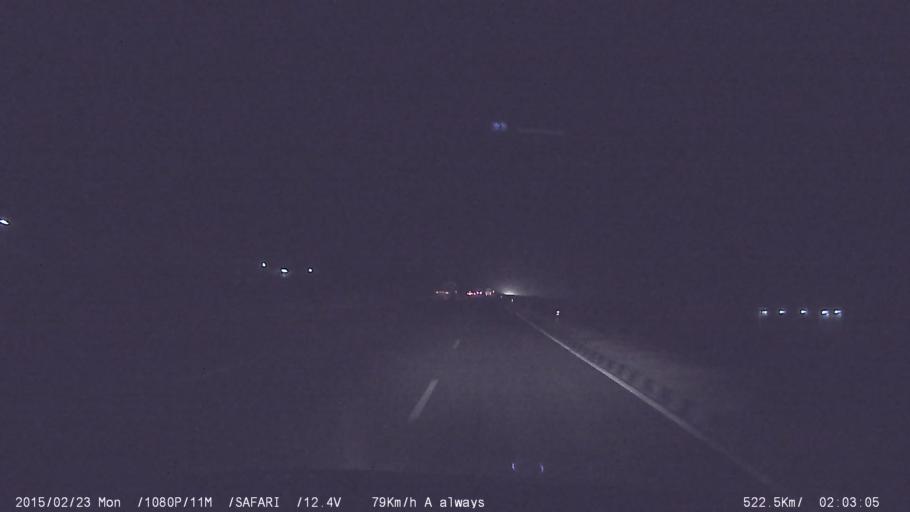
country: IN
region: Tamil Nadu
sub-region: Krishnagiri
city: Krishnagiri
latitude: 12.6422
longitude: 78.0574
